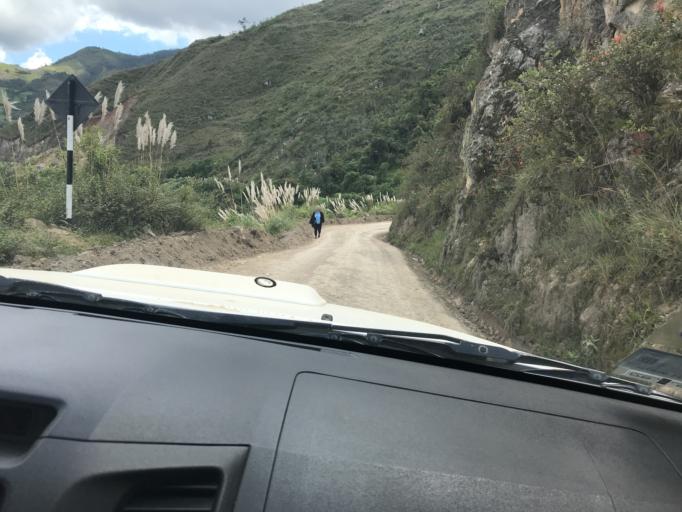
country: PE
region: Cajamarca
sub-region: Provincia de Chota
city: Querocoto
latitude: -6.3672
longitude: -79.0352
